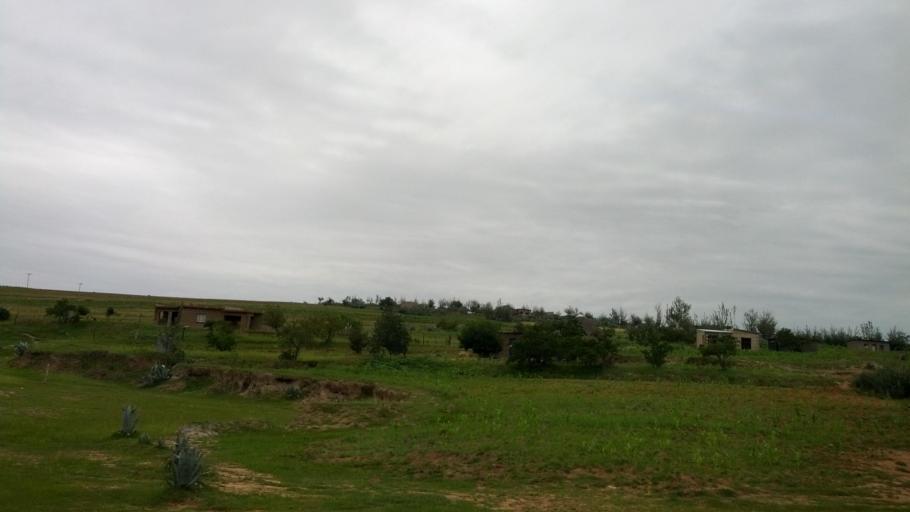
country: LS
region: Berea
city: Teyateyaneng
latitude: -29.0862
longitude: 27.8806
